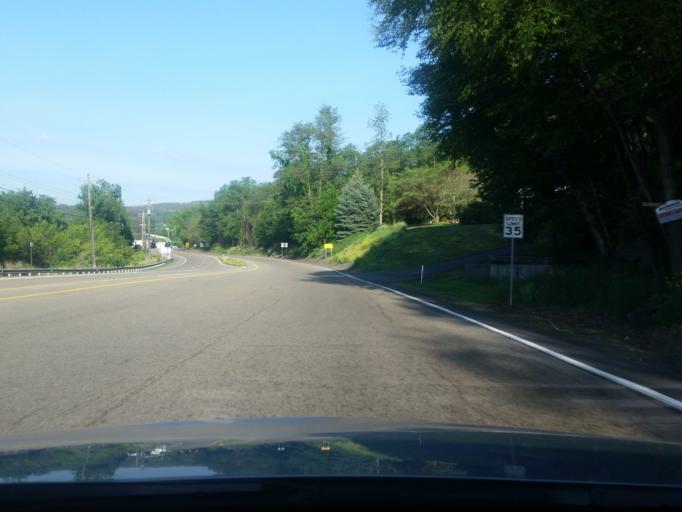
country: US
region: Pennsylvania
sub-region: Luzerne County
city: Nanticoke
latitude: 41.2177
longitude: -75.9971
